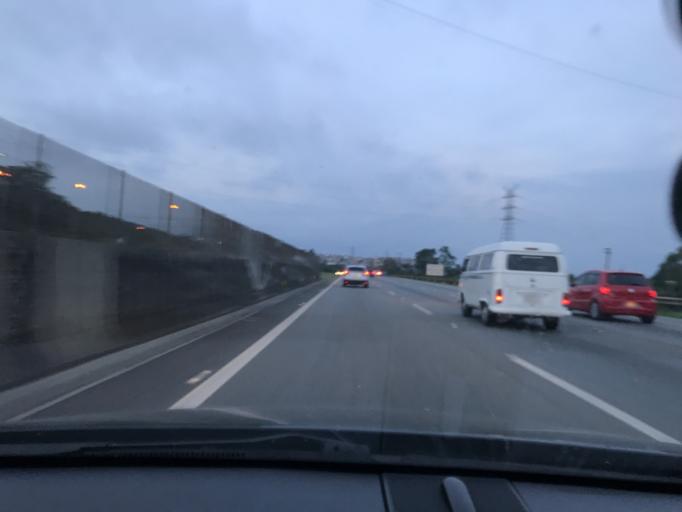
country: BR
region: Sao Paulo
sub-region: Itaquaquecetuba
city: Itaquaquecetuba
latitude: -23.4522
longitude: -46.3335
